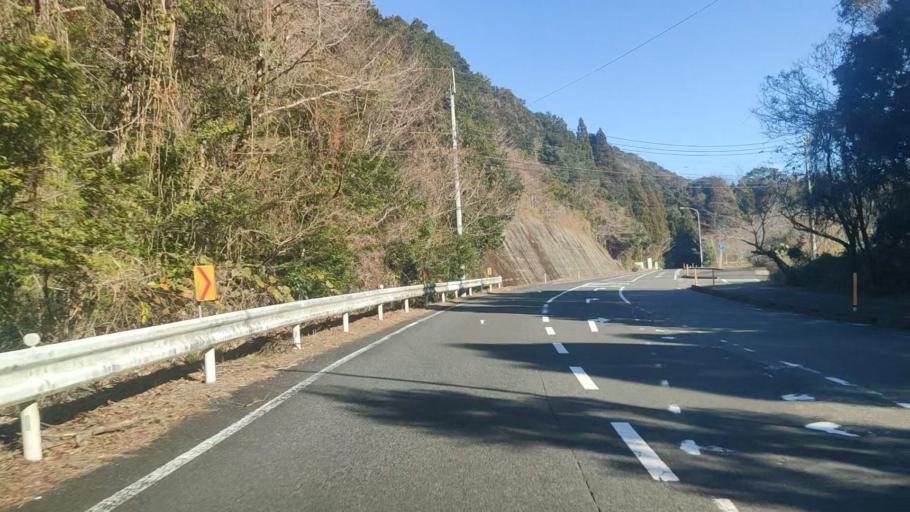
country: JP
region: Miyazaki
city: Nobeoka
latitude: 32.6960
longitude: 131.8123
